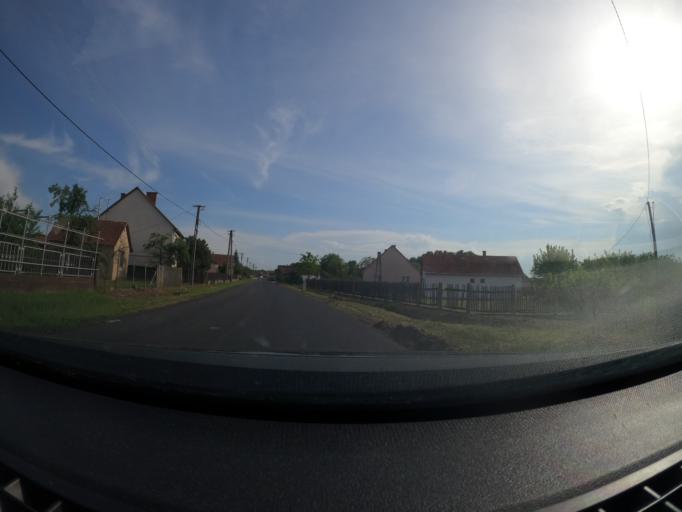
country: HU
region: Hajdu-Bihar
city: Nyirabrany
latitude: 47.5348
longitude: 22.0003
